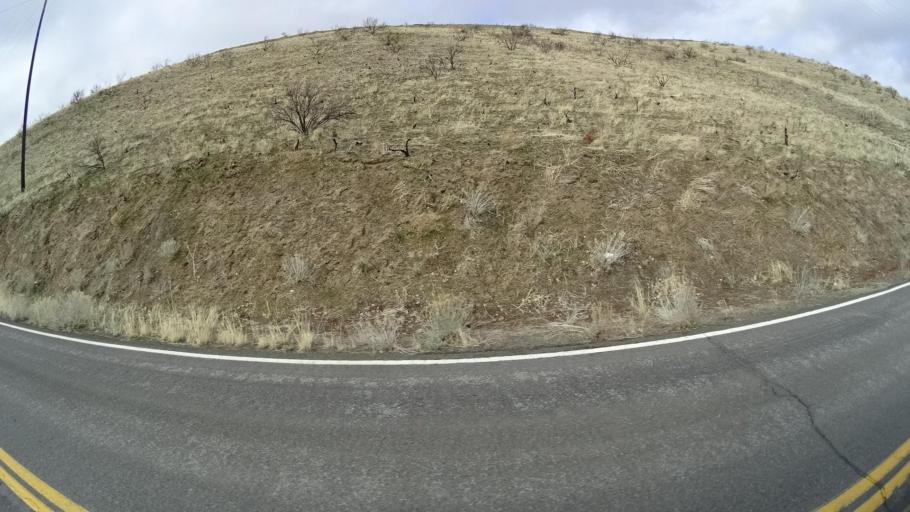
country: US
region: Nevada
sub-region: Washoe County
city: Cold Springs
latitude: 39.8405
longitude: -119.9351
